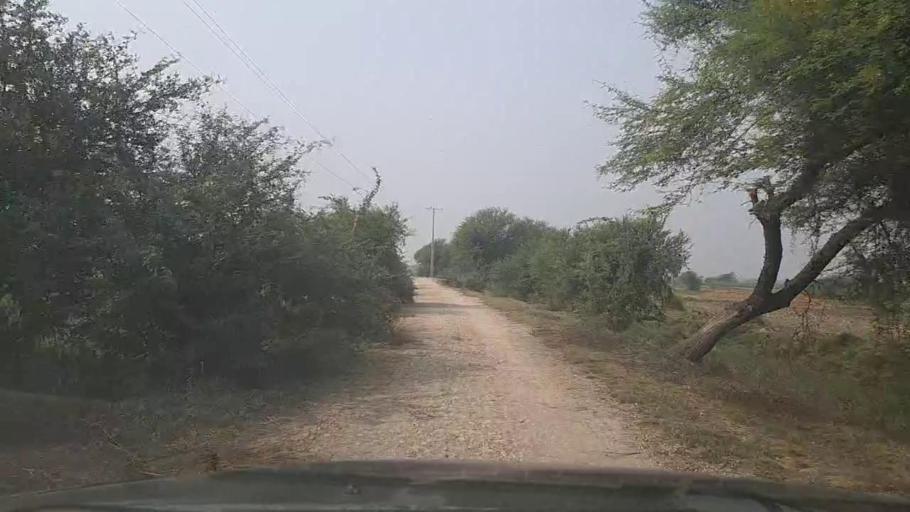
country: PK
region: Sindh
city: Mirpur Sakro
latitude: 24.5268
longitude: 67.8046
